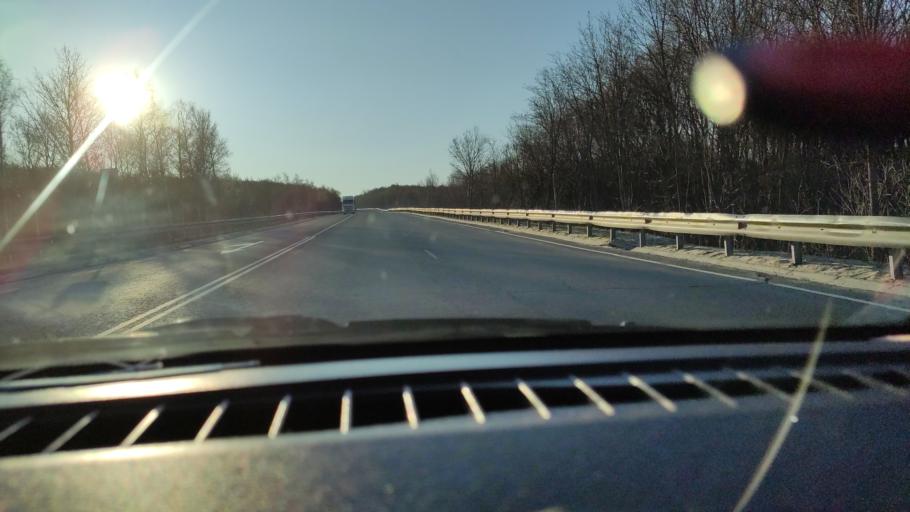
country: RU
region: Saratov
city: Vol'sk
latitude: 52.1135
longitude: 47.3141
